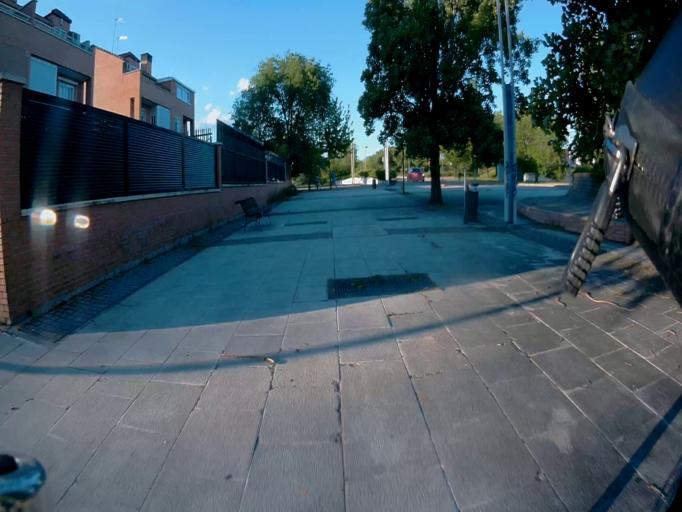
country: ES
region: Madrid
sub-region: Provincia de Madrid
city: Fuenlabrada
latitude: 40.3091
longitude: -3.7859
